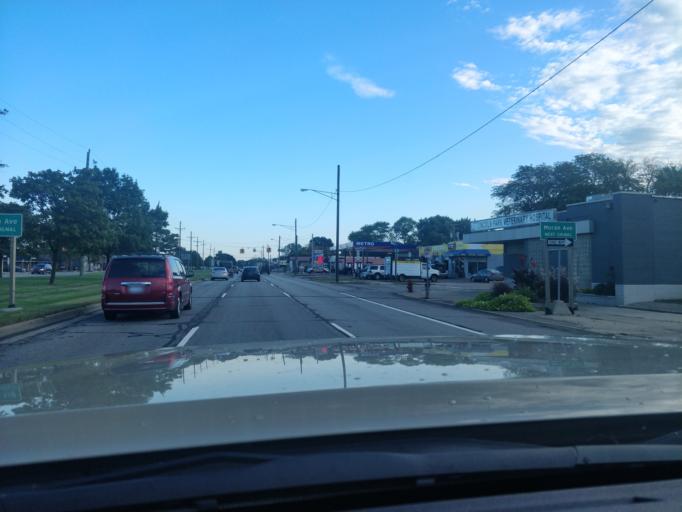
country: US
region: Michigan
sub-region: Wayne County
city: Southgate
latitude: 42.2276
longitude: -83.1808
